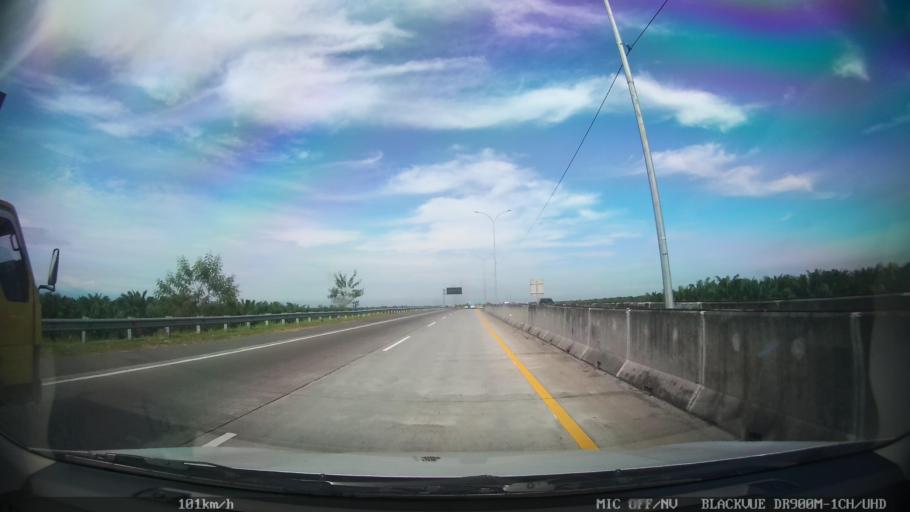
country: ID
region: North Sumatra
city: Sunggal
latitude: 3.6372
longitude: 98.5872
